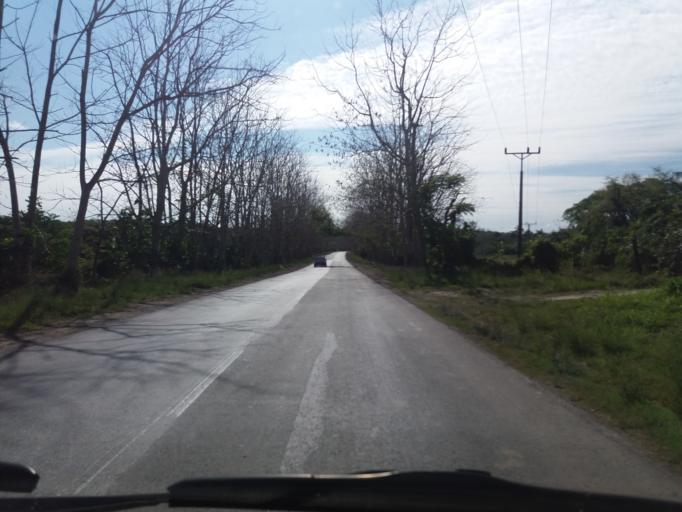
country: CU
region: Cienfuegos
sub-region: Municipio de Cienfuegos
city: Cienfuegos
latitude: 22.1654
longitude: -80.3728
